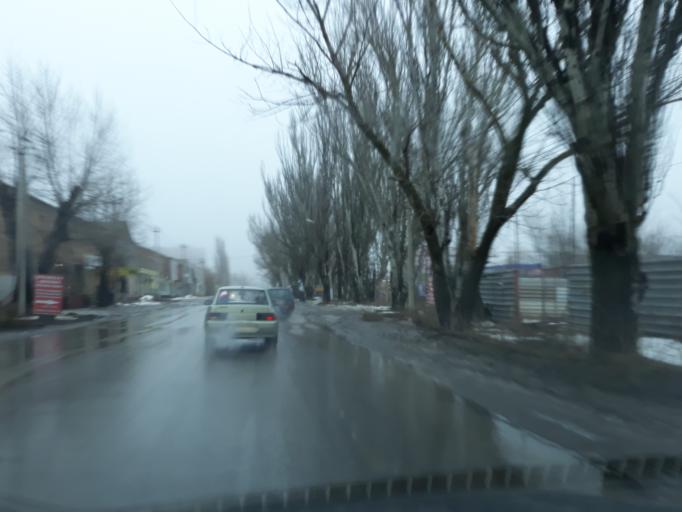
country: RU
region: Rostov
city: Taganrog
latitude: 47.2132
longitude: 38.8734
